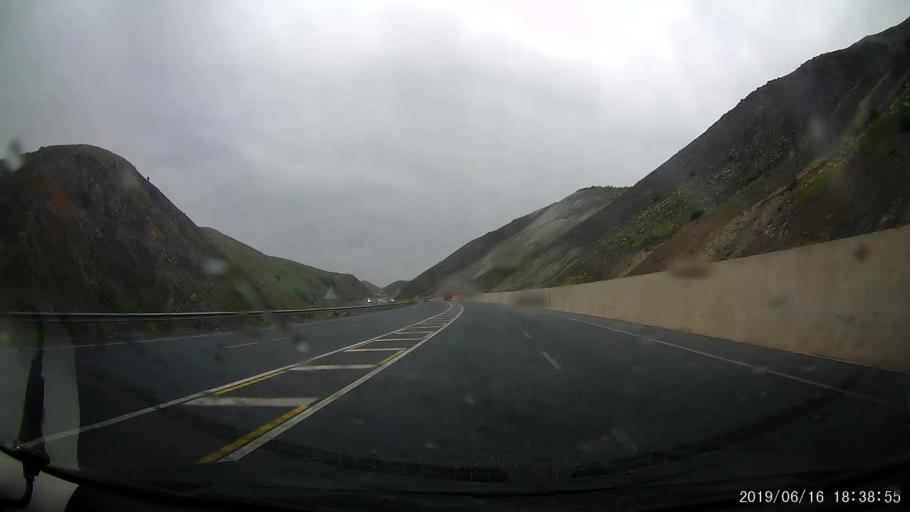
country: TR
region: Erzincan
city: Catalarmut
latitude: 39.8828
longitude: 39.1759
